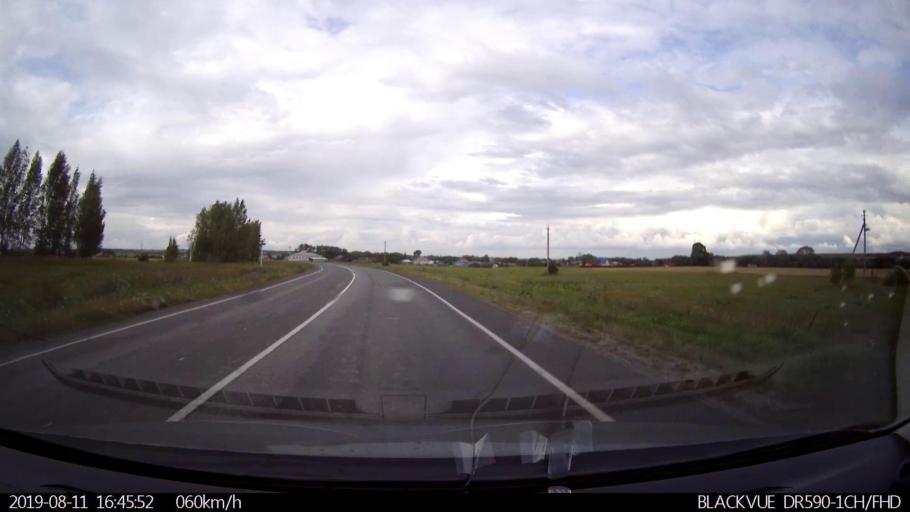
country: RU
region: Ulyanovsk
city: Mayna
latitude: 54.1940
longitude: 47.6884
